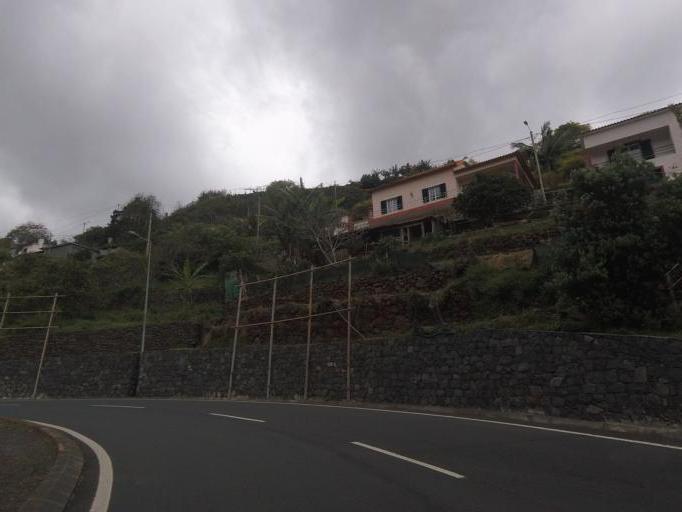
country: PT
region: Madeira
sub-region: Machico
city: Machico
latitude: 32.7316
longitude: -16.7838
